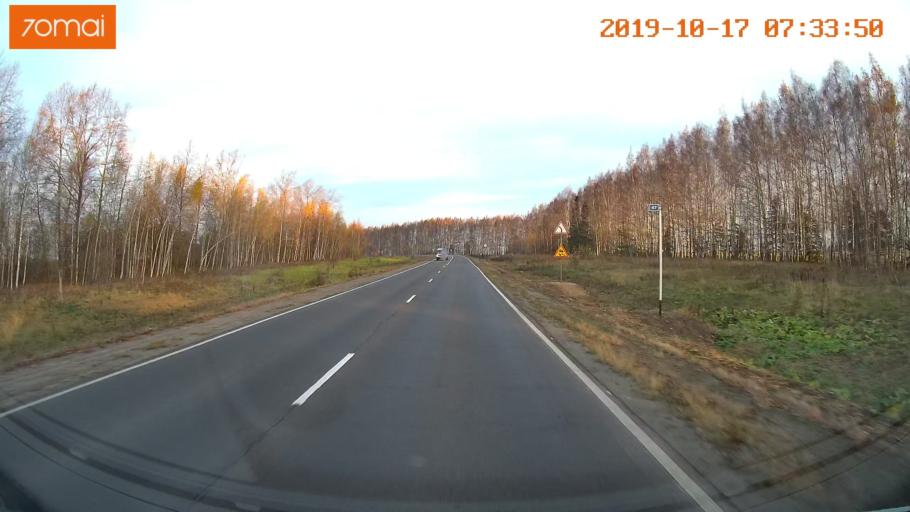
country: RU
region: Ivanovo
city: Gavrilov Posad
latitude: 56.4122
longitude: 39.9528
